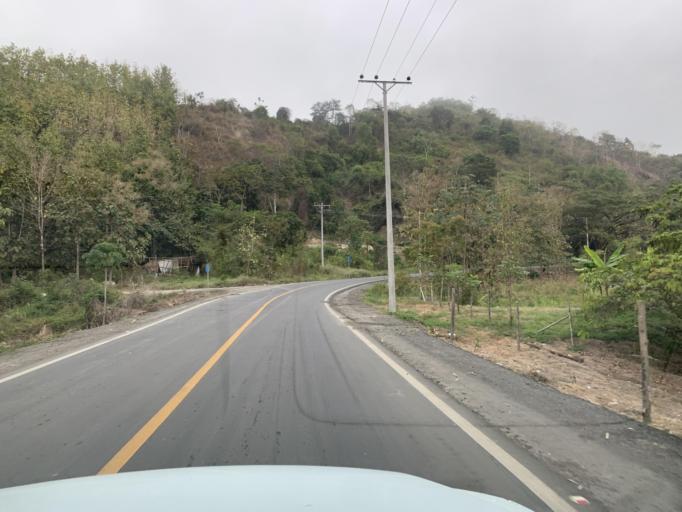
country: EC
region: Guayas
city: Coronel Marcelino Mariduena
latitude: -2.3540
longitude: -79.5295
